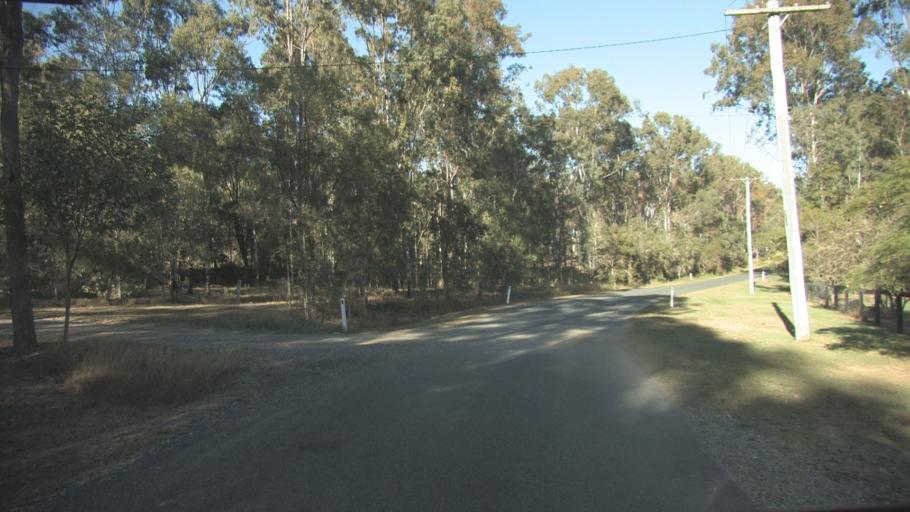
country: AU
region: Queensland
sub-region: Logan
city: North Maclean
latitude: -27.7958
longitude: 152.9949
